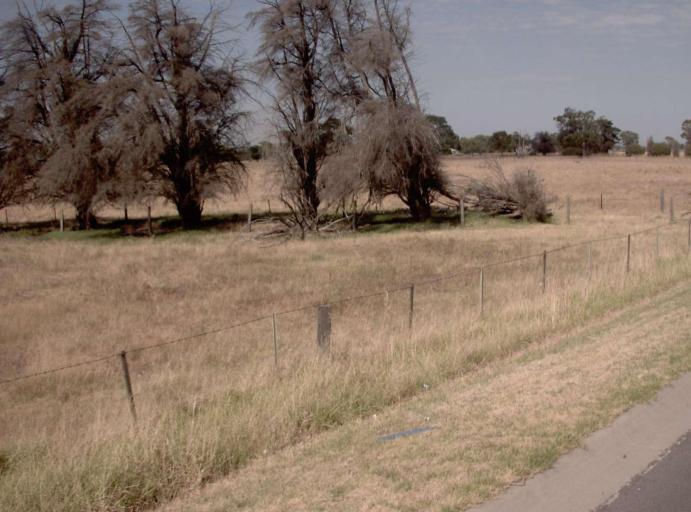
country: AU
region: Victoria
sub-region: Greater Dandenong
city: Keysborough
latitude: -38.0133
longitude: 145.1659
